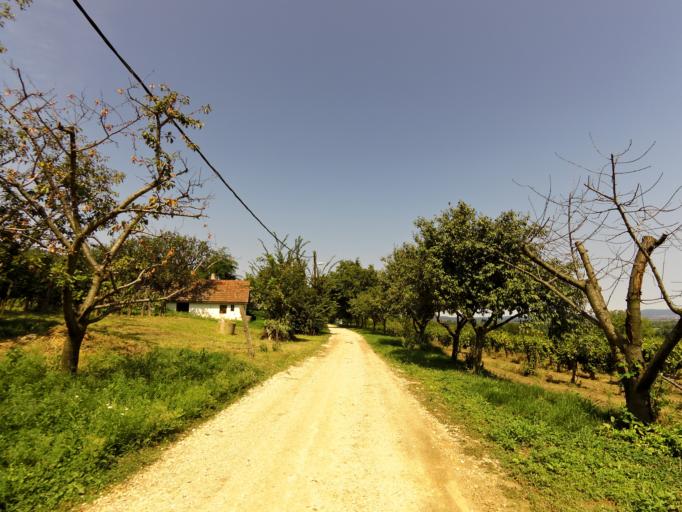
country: HU
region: Zala
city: Vonyarcvashegy
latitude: 46.8162
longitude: 17.3724
